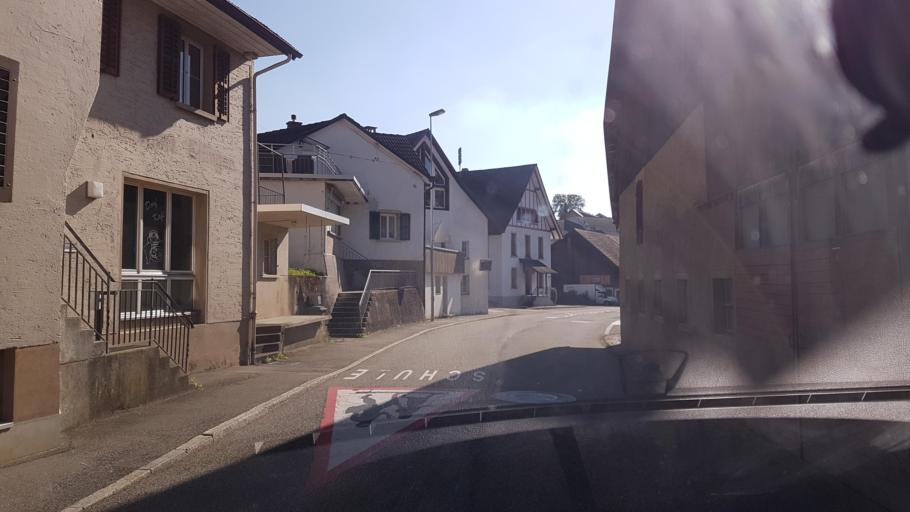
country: CH
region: Aargau
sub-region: Bezirk Laufenburg
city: Sulz
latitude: 47.5076
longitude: 8.0992
